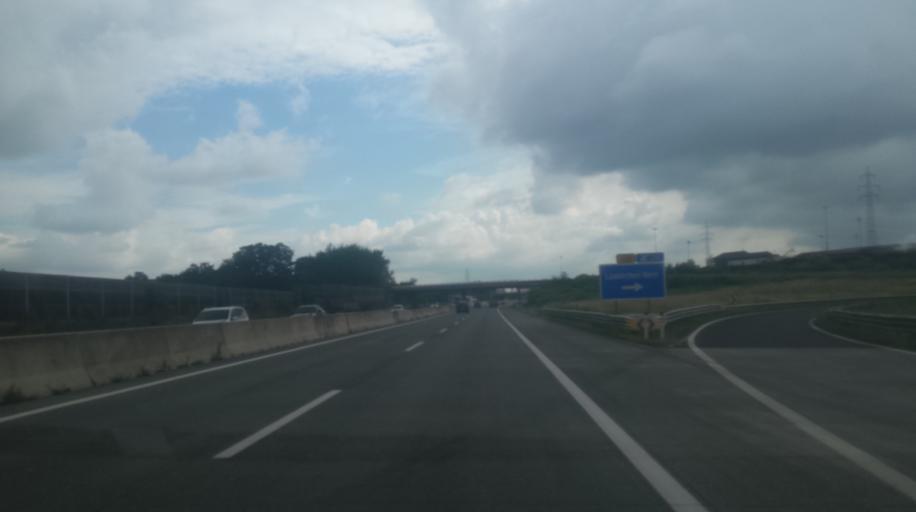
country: AT
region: Upper Austria
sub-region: Politischer Bezirk Gmunden
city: Laakirchen
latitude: 47.9979
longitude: 13.7977
